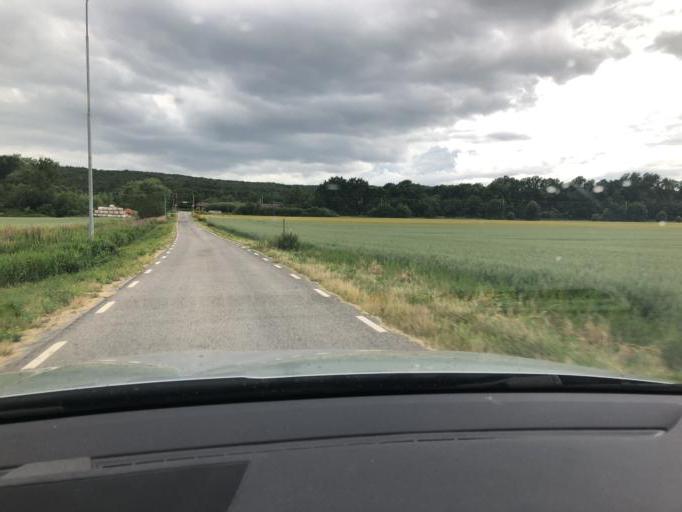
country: SE
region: Blekinge
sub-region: Solvesborgs Kommun
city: Soelvesborg
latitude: 56.1077
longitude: 14.6249
